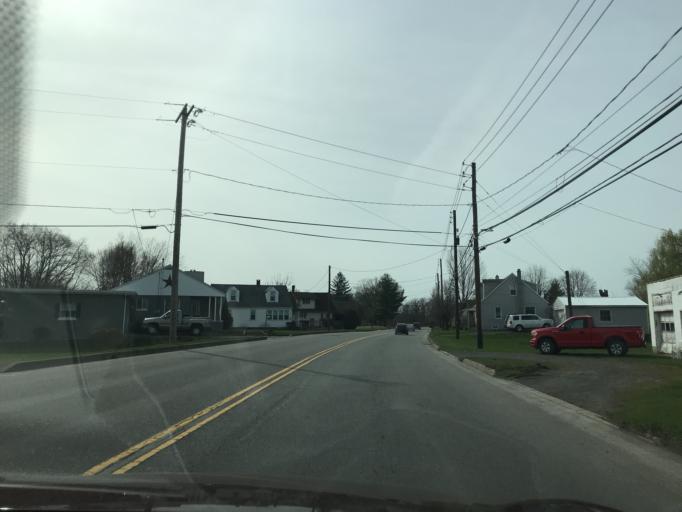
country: US
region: Pennsylvania
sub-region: Union County
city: Lewisburg
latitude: 40.9665
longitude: -76.8594
